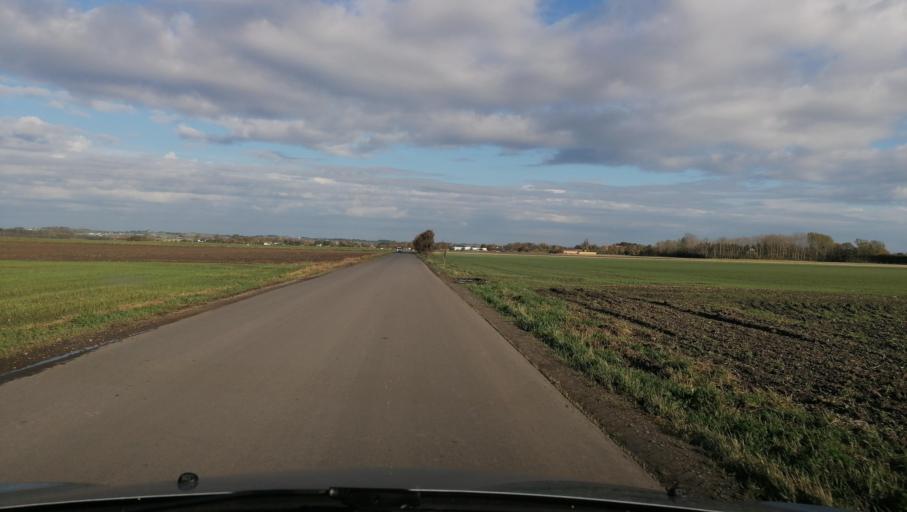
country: DK
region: Zealand
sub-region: Odsherred Kommune
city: Horve
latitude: 55.7852
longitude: 11.4438
